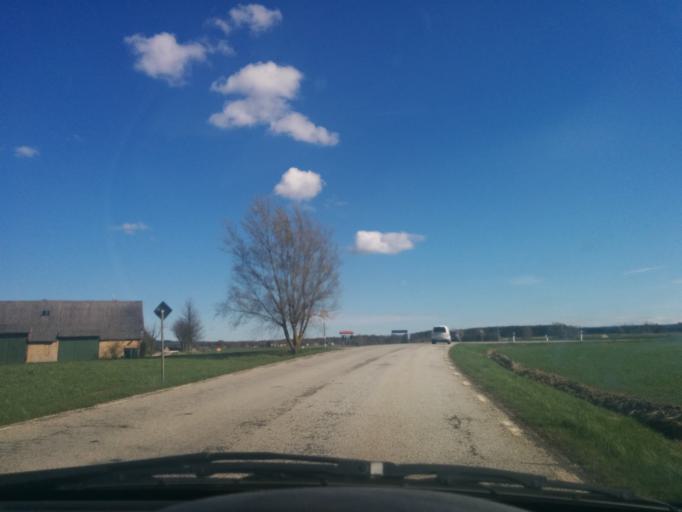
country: SE
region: Skane
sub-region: Lunds Kommun
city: Genarp
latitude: 55.6083
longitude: 13.3665
